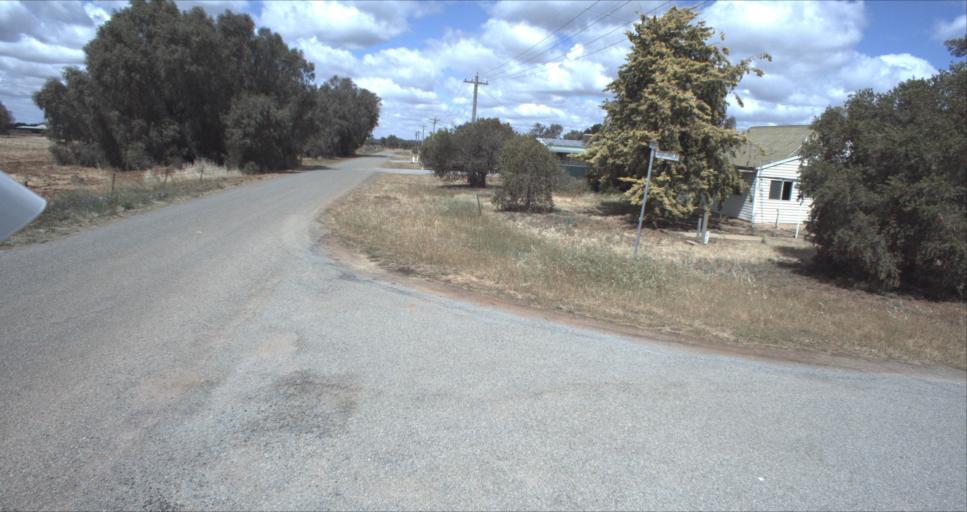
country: AU
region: New South Wales
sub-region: Murrumbidgee Shire
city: Darlington Point
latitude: -34.5204
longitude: 146.1875
